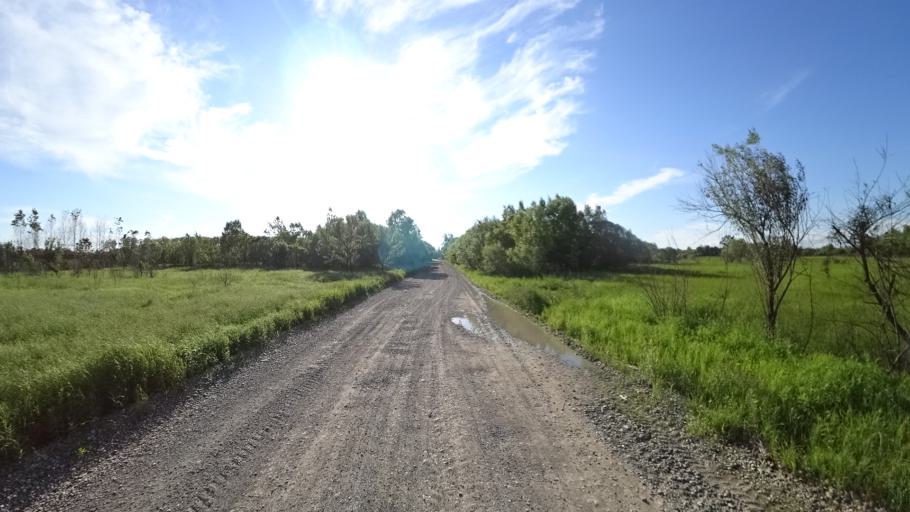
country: RU
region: Khabarovsk Krai
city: Khor
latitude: 47.8445
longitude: 134.9483
